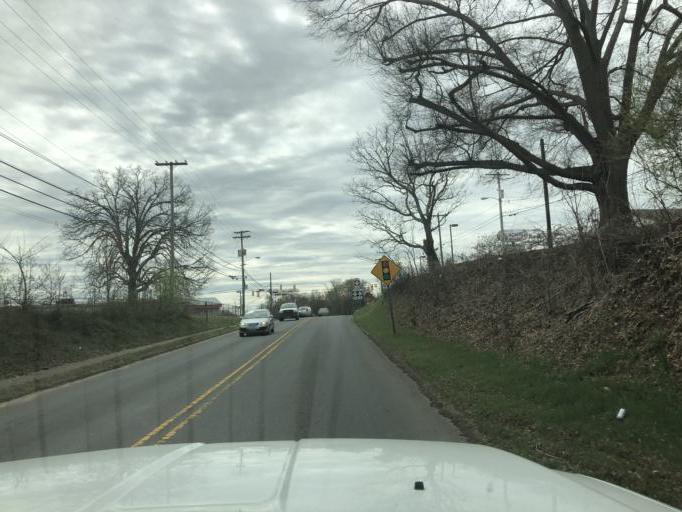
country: US
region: North Carolina
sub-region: Gaston County
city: Dallas
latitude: 35.3173
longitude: -81.1675
